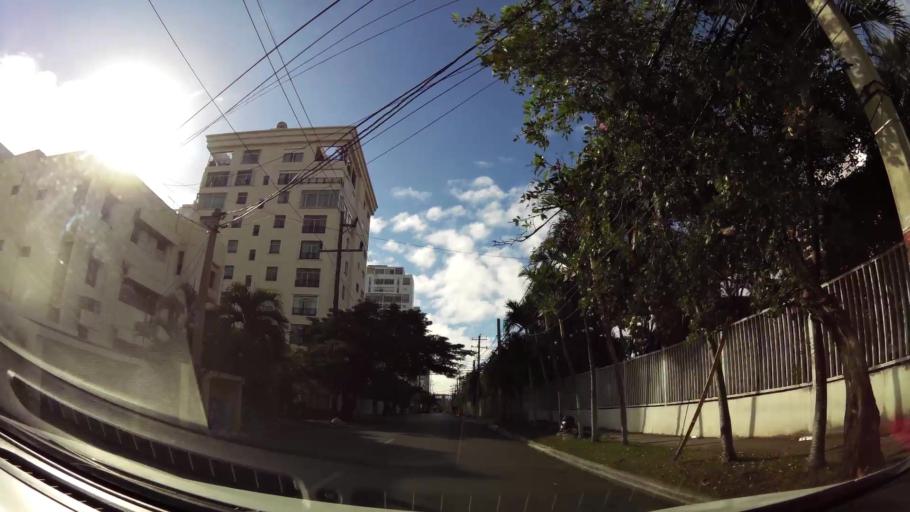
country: DO
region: Nacional
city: La Julia
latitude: 18.4702
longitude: -69.9379
